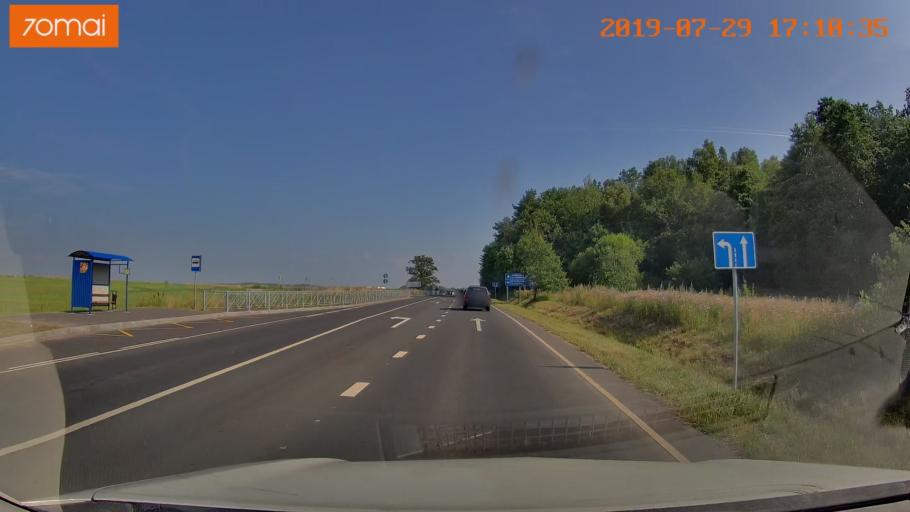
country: RU
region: Kaliningrad
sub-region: Gorod Kaliningrad
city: Kaliningrad
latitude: 54.8011
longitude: 20.3704
